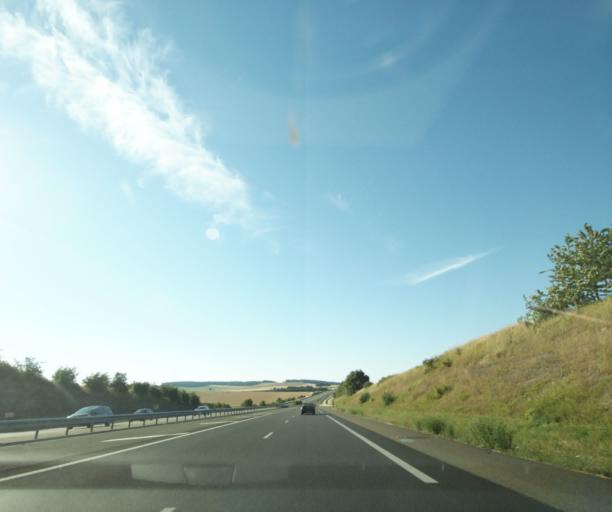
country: FR
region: Bourgogne
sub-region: Departement de l'Yonne
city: Sergines
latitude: 48.3229
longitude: 3.2306
